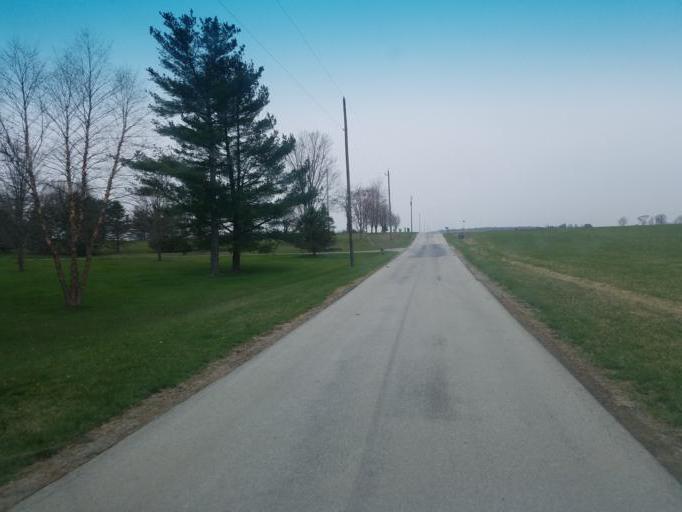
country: US
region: Ohio
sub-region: Delaware County
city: Delaware
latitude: 40.3801
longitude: -83.0900
